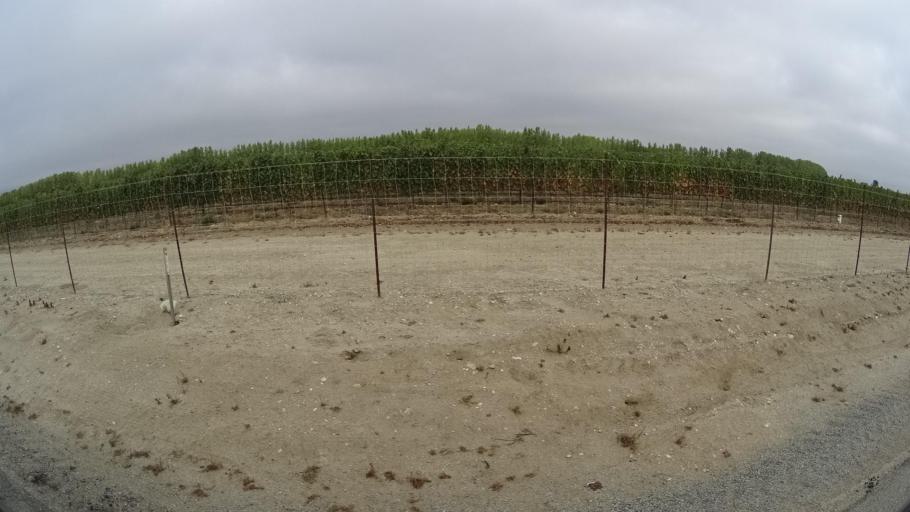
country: US
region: California
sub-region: Monterey County
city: Greenfield
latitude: 36.3249
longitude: -121.2885
